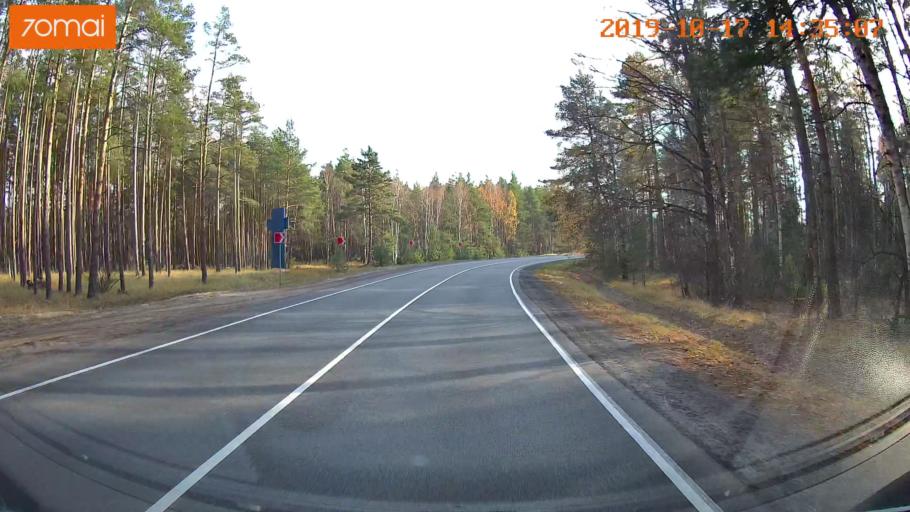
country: RU
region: Rjazan
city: Solotcha
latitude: 54.9038
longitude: 40.0032
